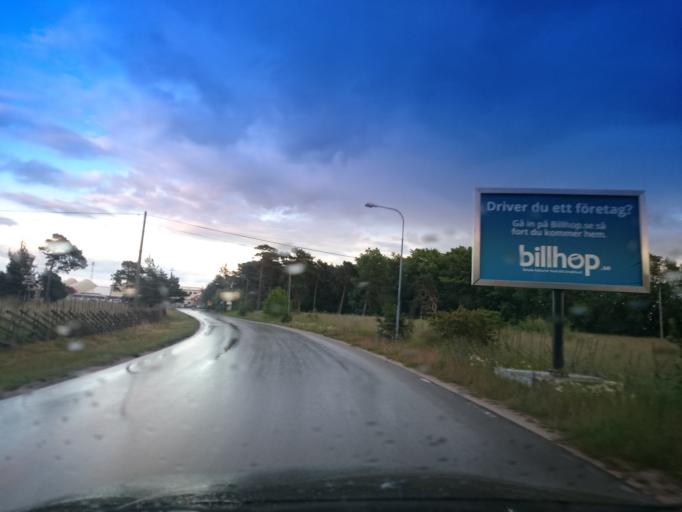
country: SE
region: Gotland
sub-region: Gotland
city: Visby
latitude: 57.6607
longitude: 18.3343
